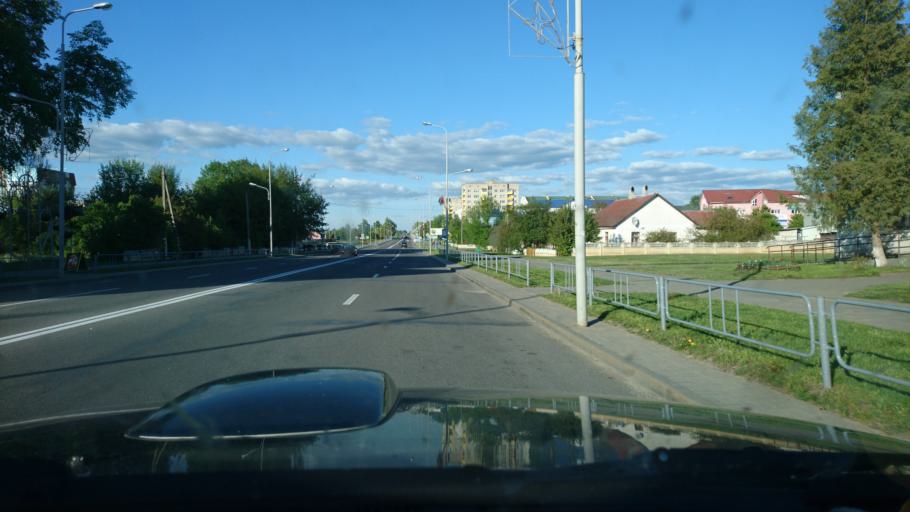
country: BY
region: Brest
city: Ivatsevichy
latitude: 52.7111
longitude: 25.3417
